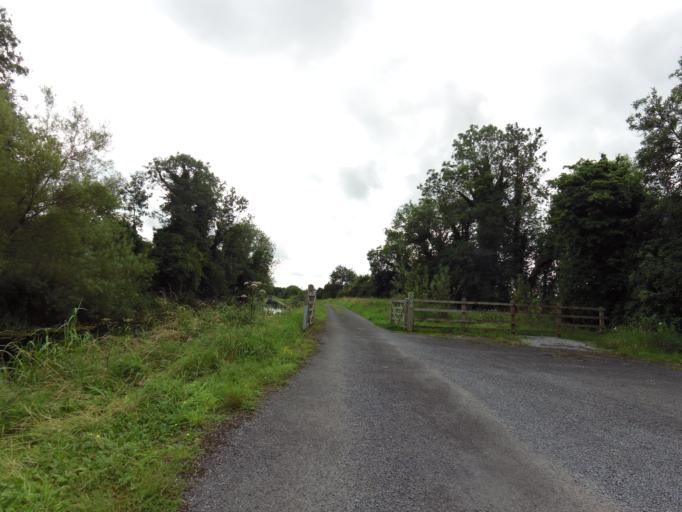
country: IE
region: Leinster
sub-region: An Iarmhi
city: An Muileann gCearr
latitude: 53.5454
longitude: -7.4740
